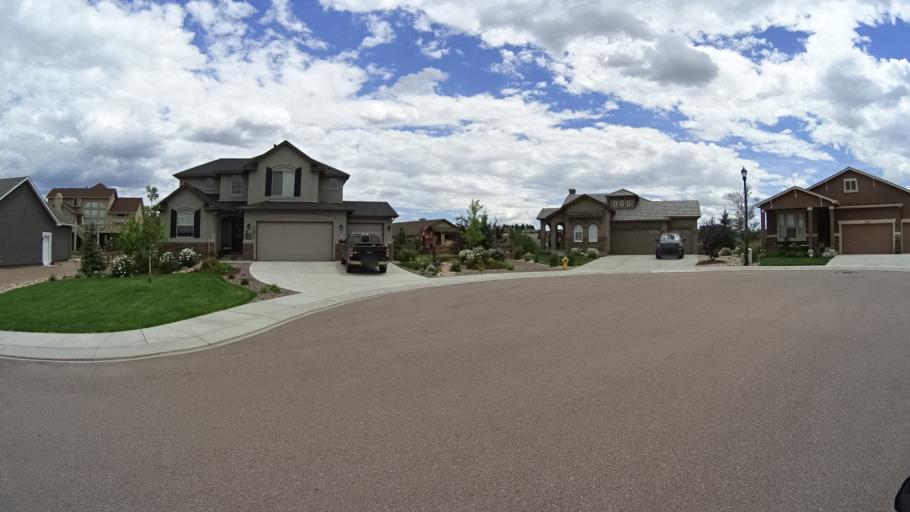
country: US
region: Colorado
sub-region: El Paso County
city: Gleneagle
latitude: 39.0211
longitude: -104.8063
